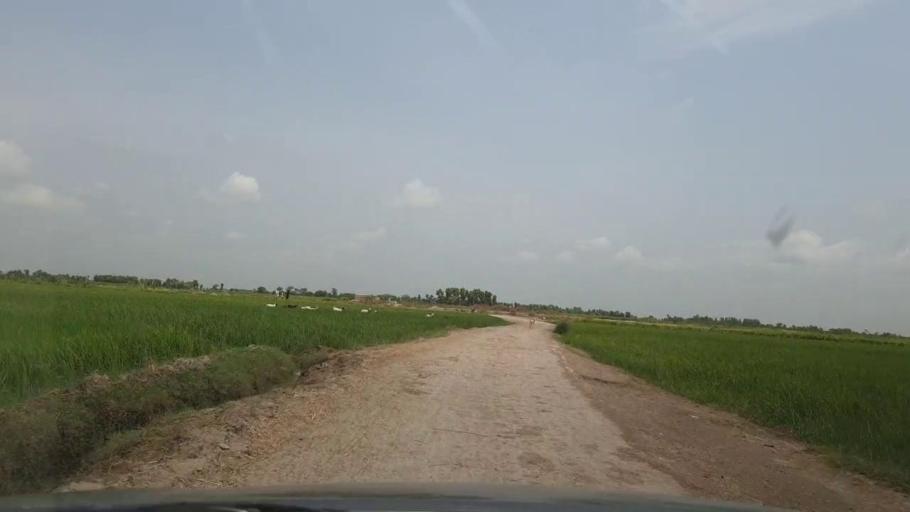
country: PK
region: Sindh
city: Ratodero
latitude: 27.9153
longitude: 68.2983
